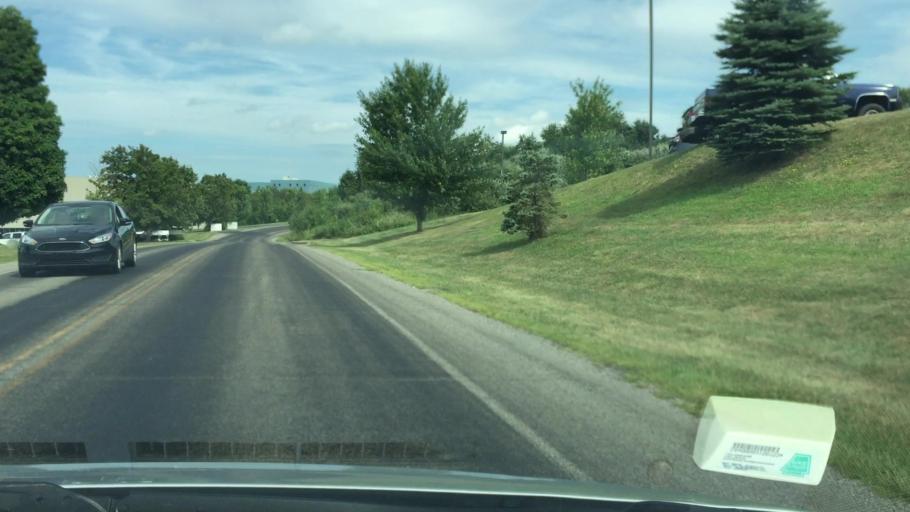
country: US
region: Pennsylvania
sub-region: Armstrong County
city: Apollo
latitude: 40.5314
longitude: -79.6484
